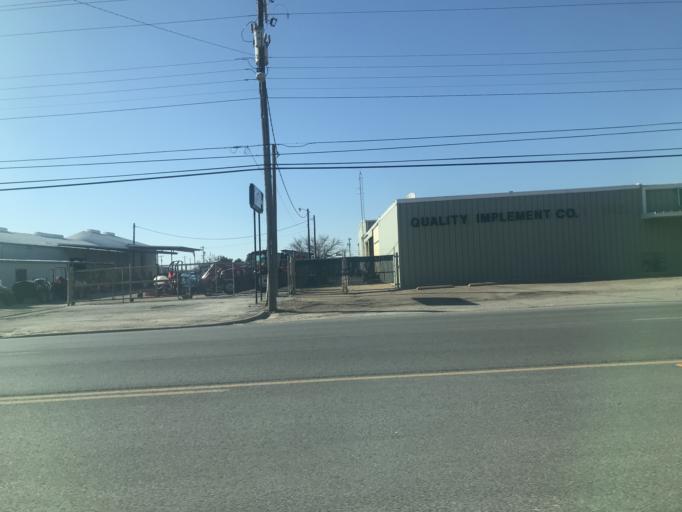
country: US
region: Texas
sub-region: Taylor County
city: Abilene
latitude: 32.4090
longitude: -99.7424
